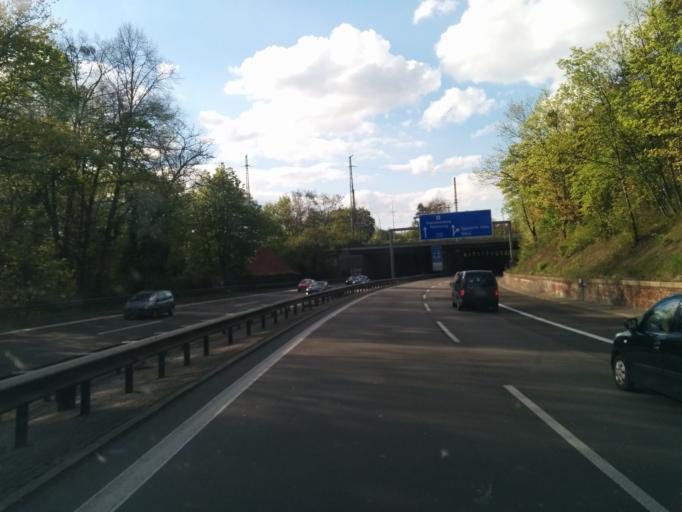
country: DE
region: Berlin
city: Nikolassee
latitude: 52.4257
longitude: 13.1923
